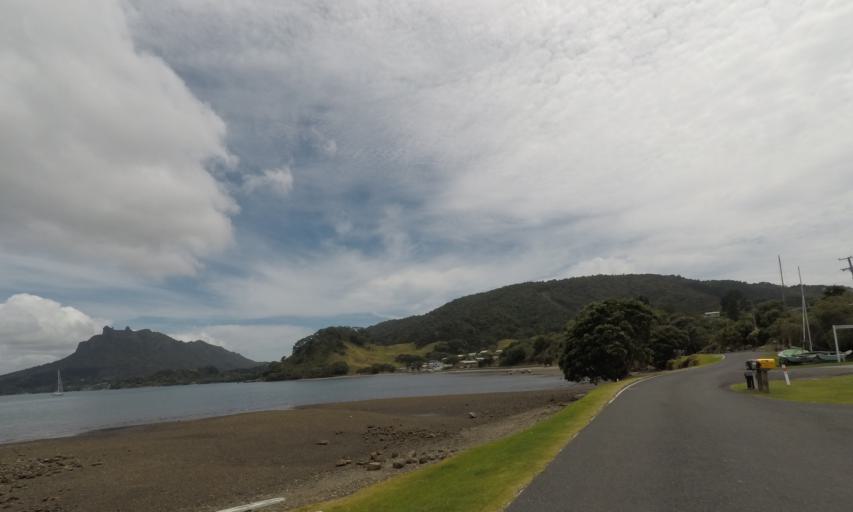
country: NZ
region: Northland
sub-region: Whangarei
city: Ruakaka
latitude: -35.8460
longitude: 174.5355
